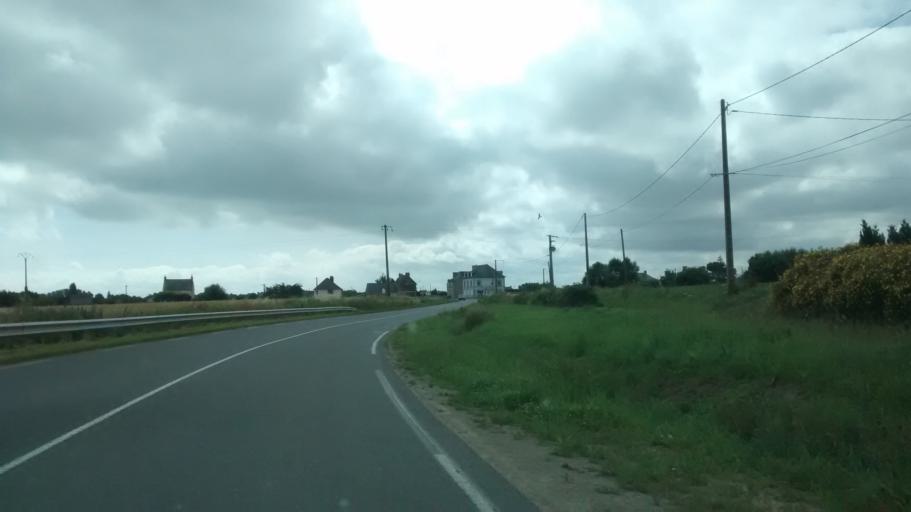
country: FR
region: Brittany
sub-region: Departement d'Ille-et-Vilaine
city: Saint-Meloir-des-Ondes
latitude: 48.6495
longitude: -1.9069
